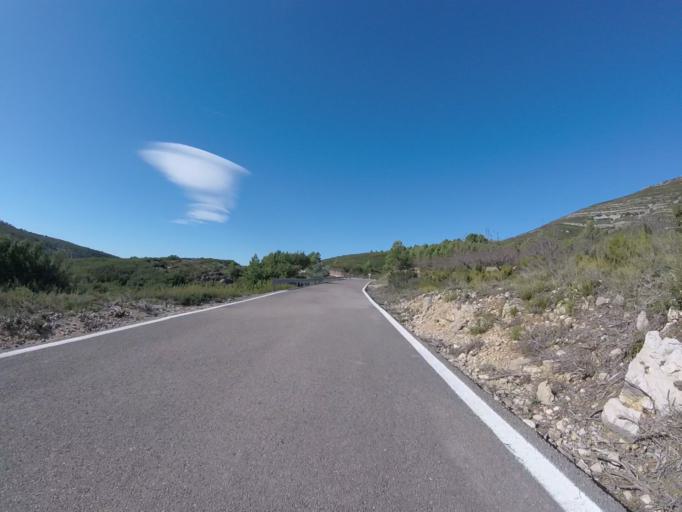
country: ES
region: Valencia
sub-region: Provincia de Castello
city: Albocasser
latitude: 40.3918
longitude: 0.0383
